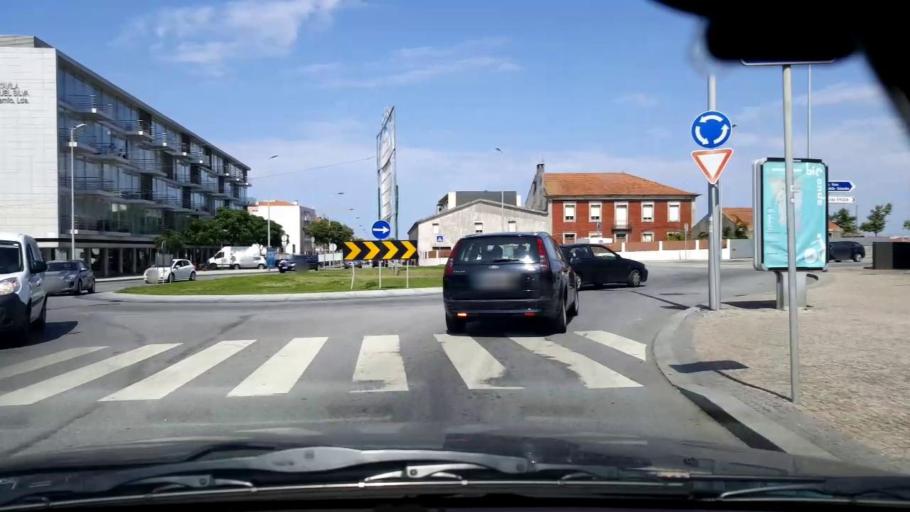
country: PT
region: Porto
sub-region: Vila do Conde
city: Vila do Conde
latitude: 41.3673
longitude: -8.7503
